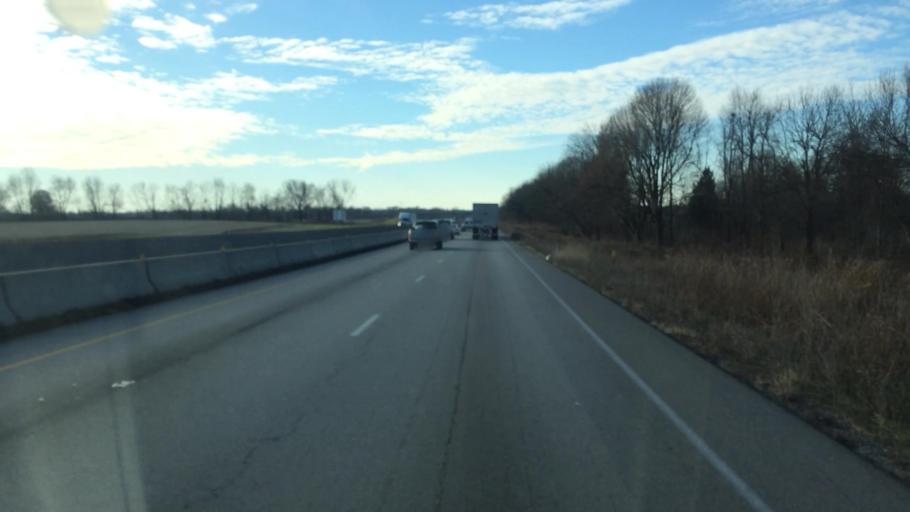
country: US
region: Kentucky
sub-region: Hardin County
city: Elizabethtown
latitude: 37.5795
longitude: -85.8725
